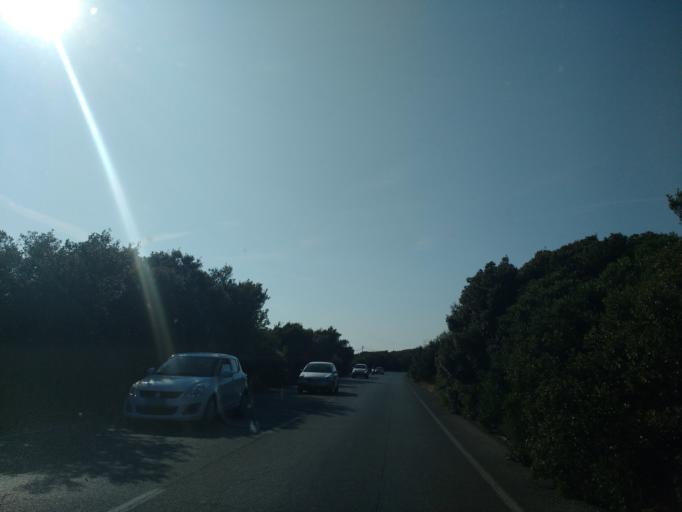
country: IT
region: Latium
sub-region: Citta metropolitana di Roma Capitale
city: Acilia-Castel Fusano-Ostia Antica
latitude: 41.6902
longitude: 12.3692
